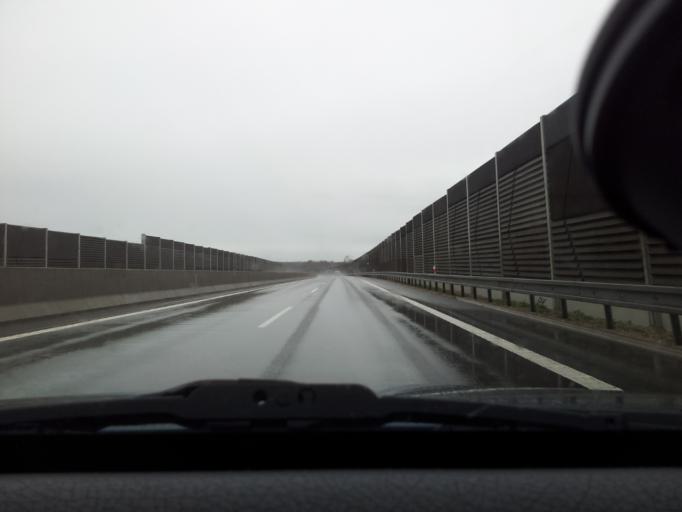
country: SK
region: Nitriansky
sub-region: Okres Nitra
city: Nitra
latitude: 48.2924
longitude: 18.0417
